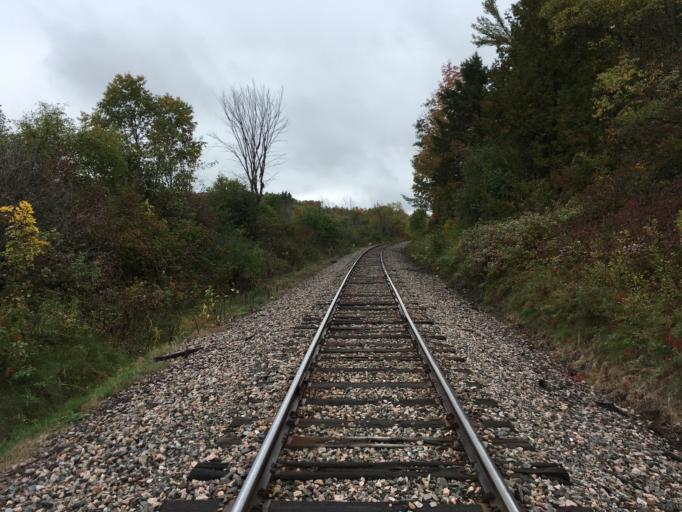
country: US
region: Vermont
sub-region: Orleans County
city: Newport
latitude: 44.8660
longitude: -72.2051
